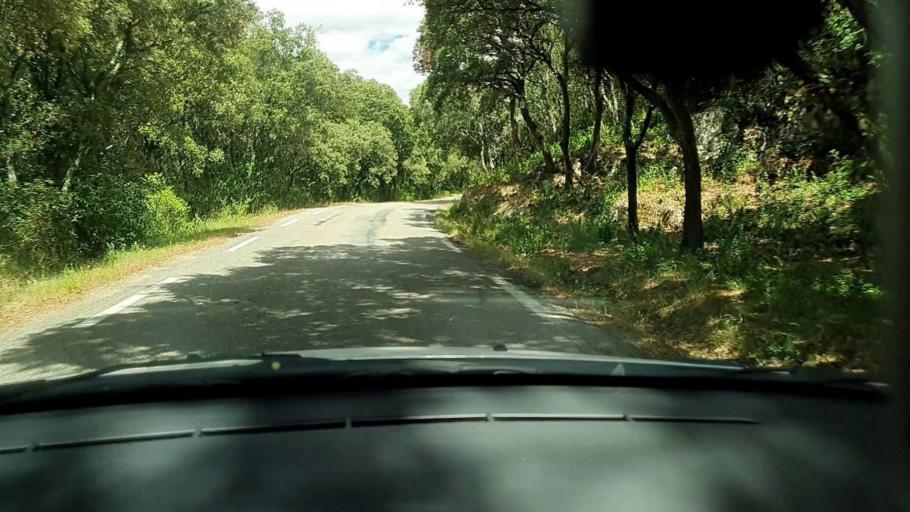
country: FR
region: Languedoc-Roussillon
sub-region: Departement du Gard
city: Cabrieres
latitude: 43.9269
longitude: 4.4717
